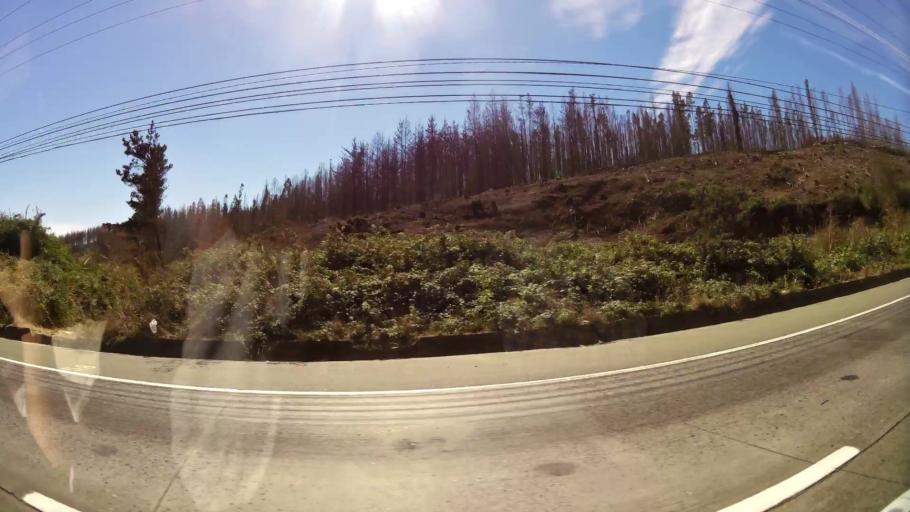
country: CL
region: Biobio
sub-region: Provincia de Concepcion
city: Penco
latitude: -36.7631
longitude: -73.0089
